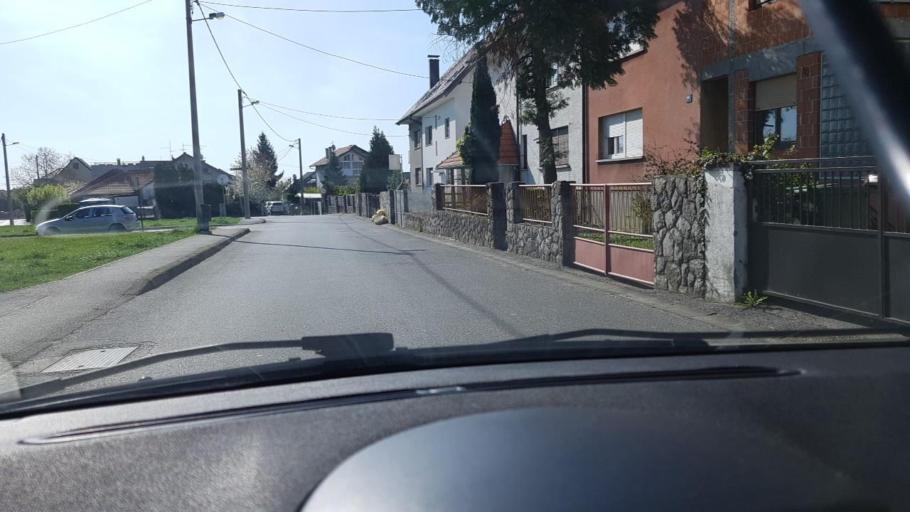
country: HR
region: Grad Zagreb
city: Zagreb
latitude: 45.8305
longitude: 15.9992
